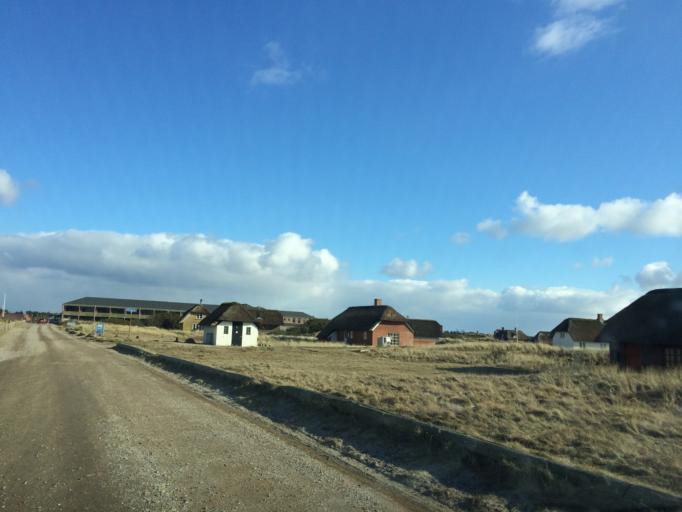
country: DK
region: Central Jutland
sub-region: Holstebro Kommune
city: Ulfborg
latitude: 56.2570
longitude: 8.1354
